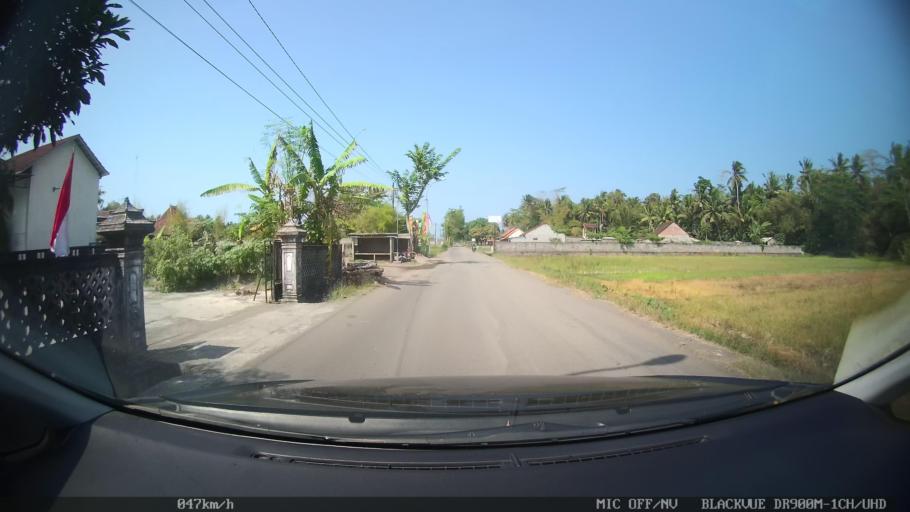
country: ID
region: Daerah Istimewa Yogyakarta
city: Srandakan
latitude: -7.9510
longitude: 110.2190
